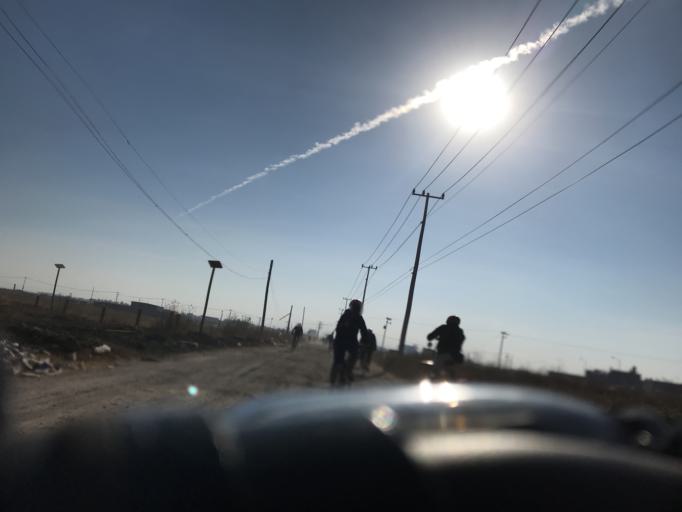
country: MX
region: Mexico
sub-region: Nextlalpan
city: Ex-Hacienda Santa Ines
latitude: 19.6965
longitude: -99.0727
